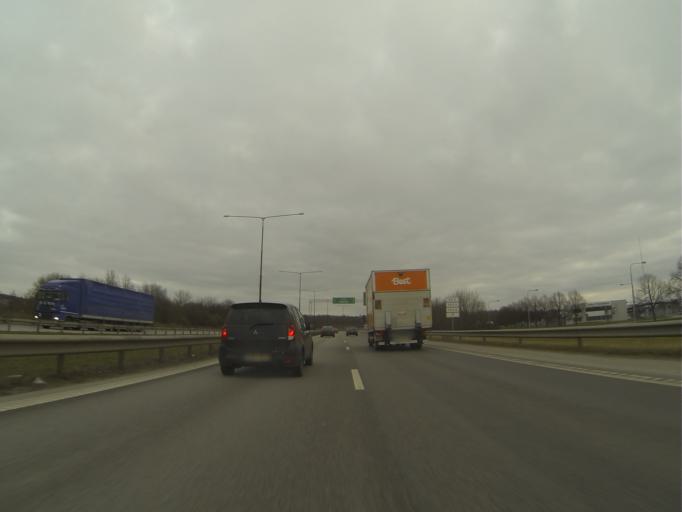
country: SE
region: Skane
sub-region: Burlovs Kommun
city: Arloev
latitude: 55.6066
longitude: 13.0674
